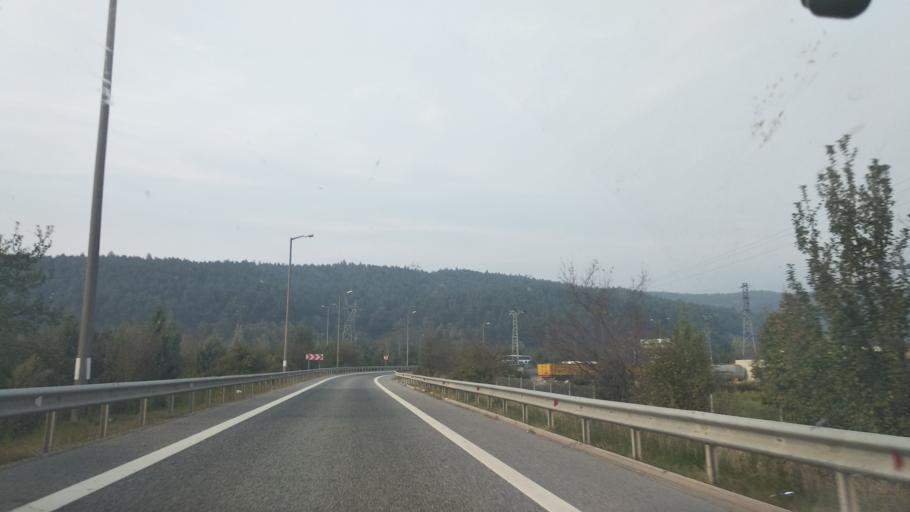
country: TR
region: Duzce
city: Kaynasli
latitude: 40.7857
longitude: 31.2770
